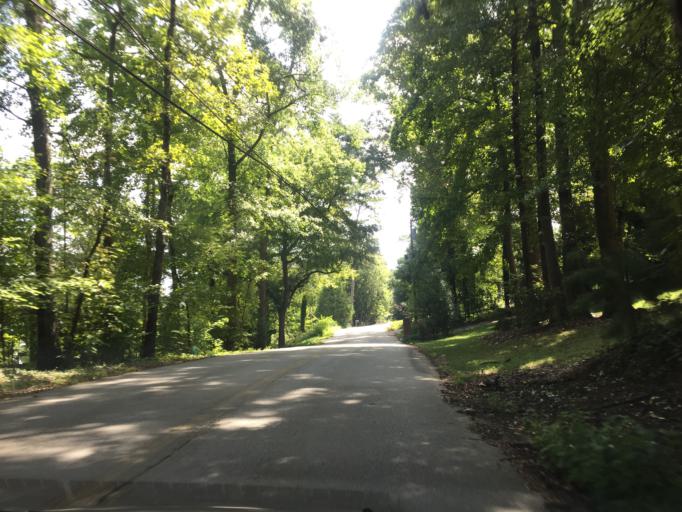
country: US
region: Tennessee
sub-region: Hamilton County
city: East Chattanooga
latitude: 35.0979
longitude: -85.1997
